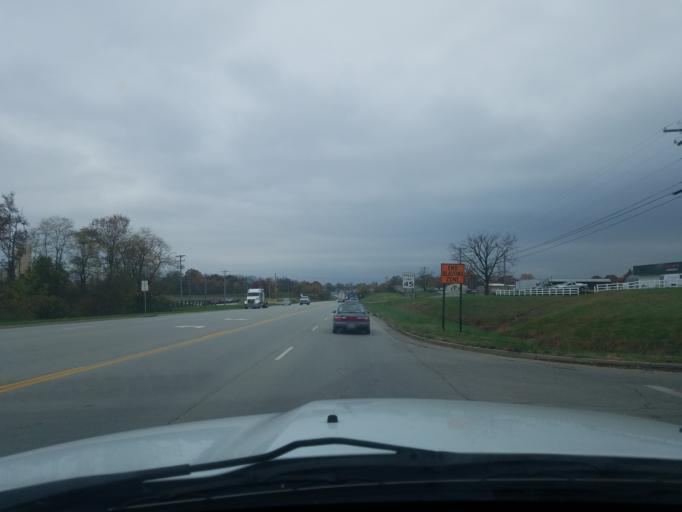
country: US
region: Kentucky
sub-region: Nelson County
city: Bardstown
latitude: 37.8220
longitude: -85.4461
